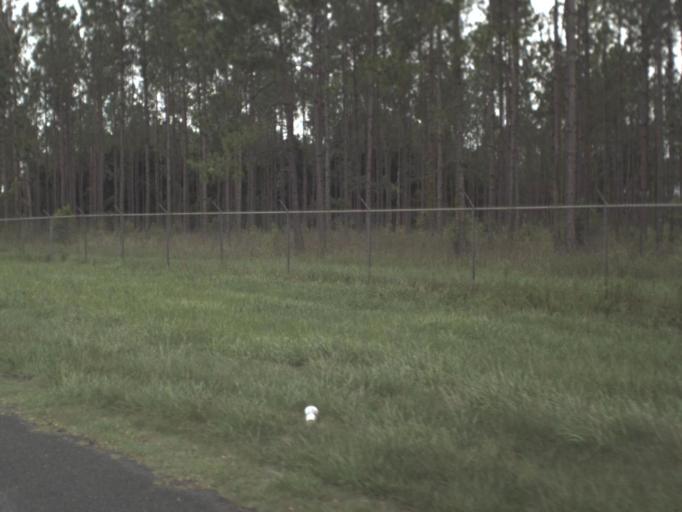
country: US
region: Florida
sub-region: Levy County
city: Williston
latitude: 29.3670
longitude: -82.4558
